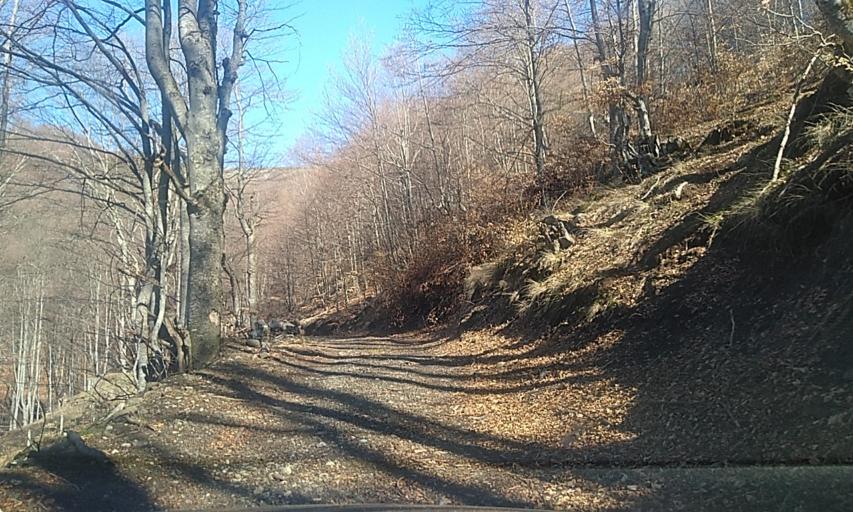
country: RS
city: Radovnica
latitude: 42.3508
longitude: 22.3393
